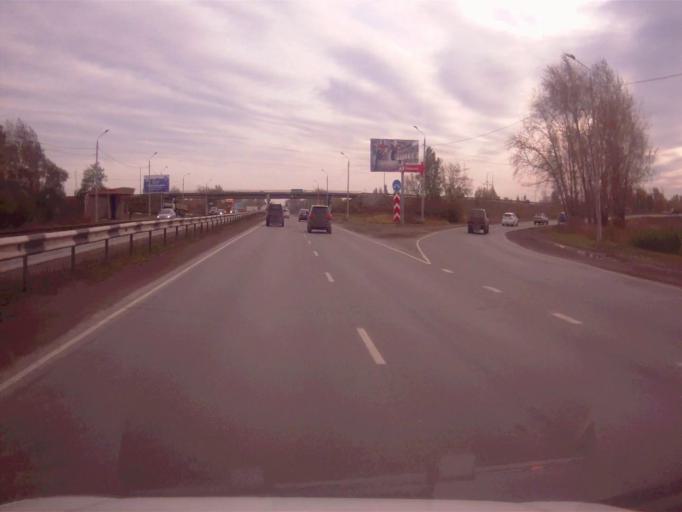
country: RU
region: Chelyabinsk
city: Novosineglazovskiy
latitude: 55.0637
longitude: 61.3983
